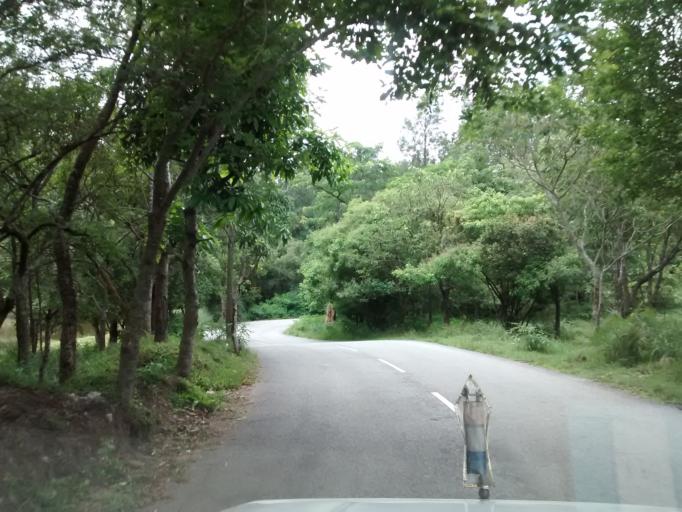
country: IN
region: Andhra Pradesh
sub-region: Chittoor
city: Tirumala
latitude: 13.6844
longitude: 79.3327
